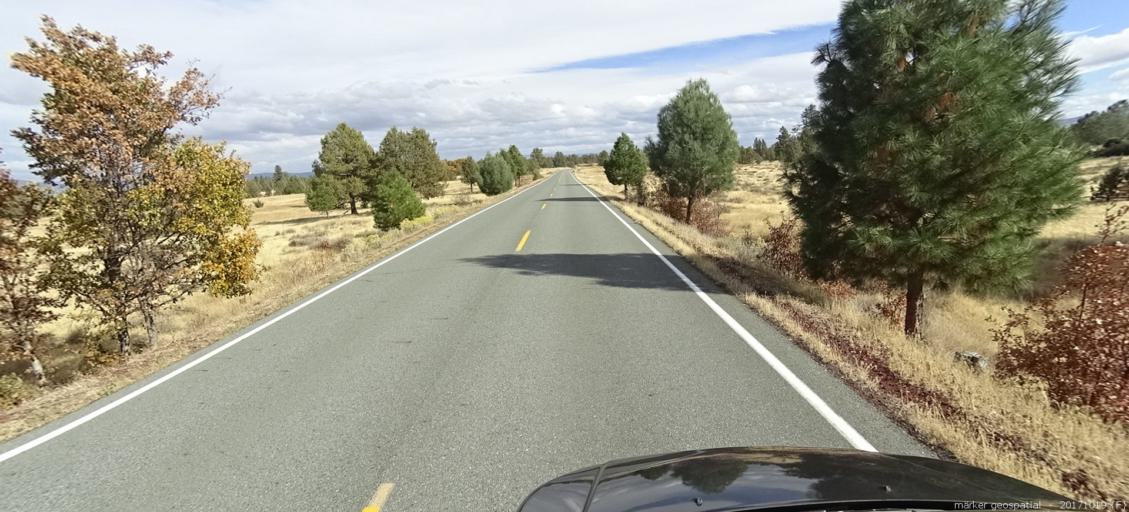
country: US
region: California
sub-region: Shasta County
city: Burney
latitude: 41.0084
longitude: -121.4614
